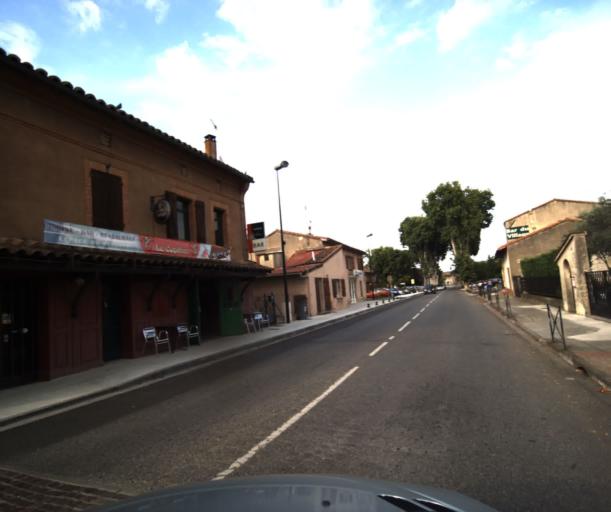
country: FR
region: Midi-Pyrenees
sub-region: Departement de la Haute-Garonne
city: Labarthe-sur-Leze
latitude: 43.4522
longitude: 1.3999
